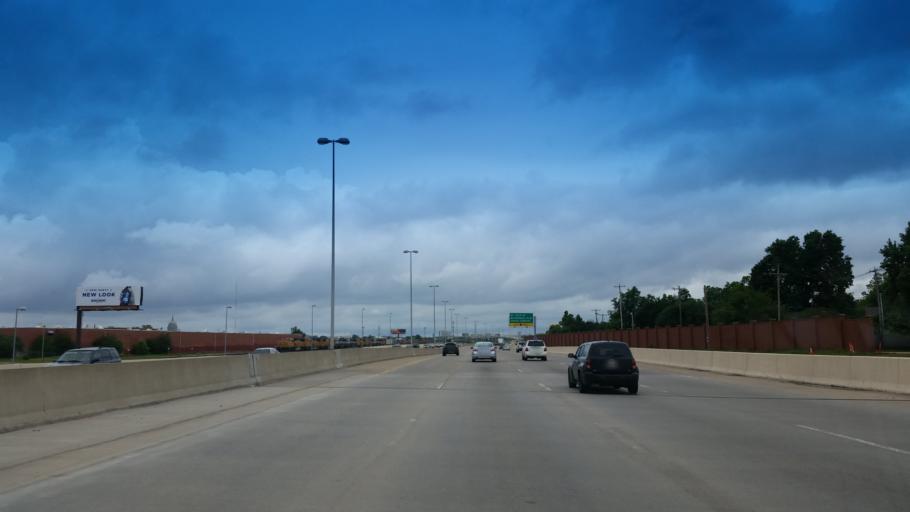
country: US
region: Oklahoma
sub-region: Oklahoma County
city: Oklahoma City
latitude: 35.5085
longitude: -97.5147
